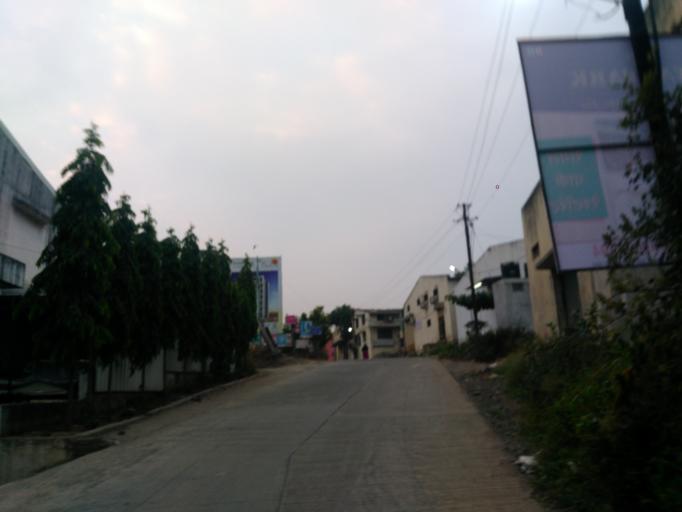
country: IN
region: Maharashtra
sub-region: Pune Division
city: Pune
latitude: 18.4494
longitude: 73.8979
